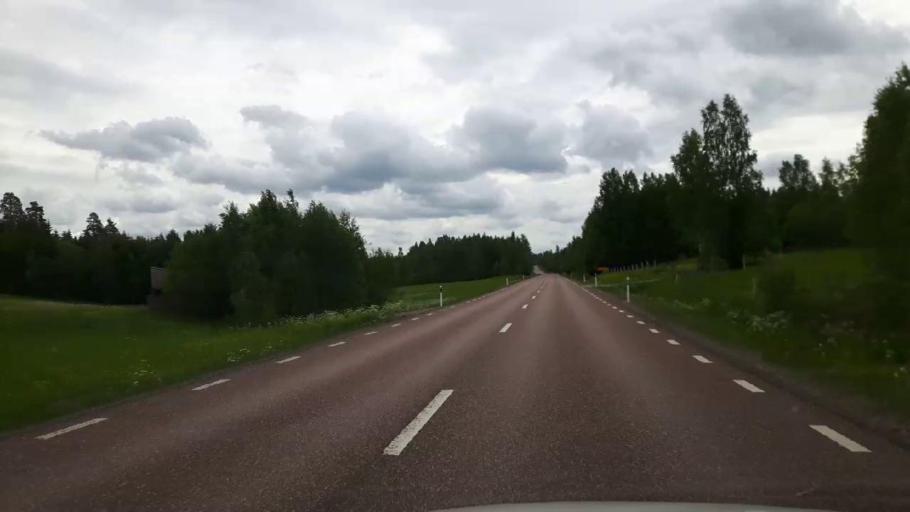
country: SE
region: Dalarna
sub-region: Hedemora Kommun
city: Brunna
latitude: 60.2042
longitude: 15.9932
